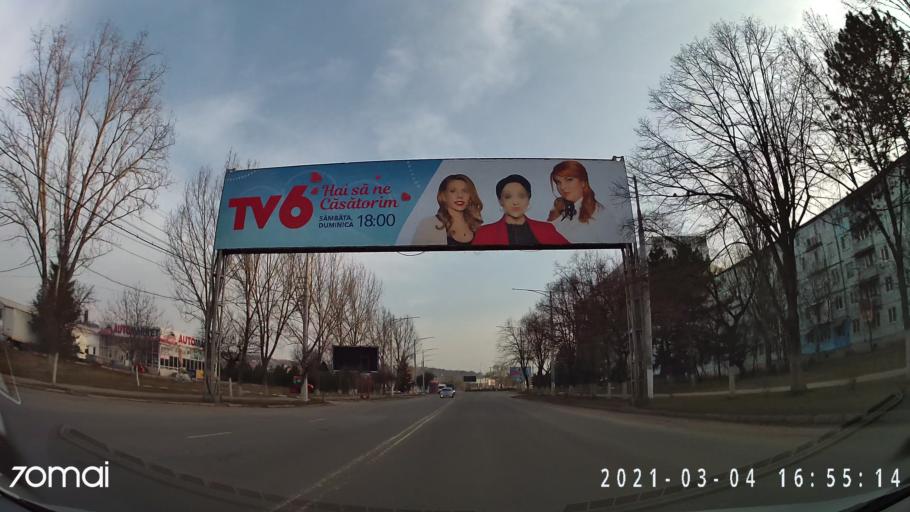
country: MD
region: Balti
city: Balti
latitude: 47.7578
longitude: 27.9410
